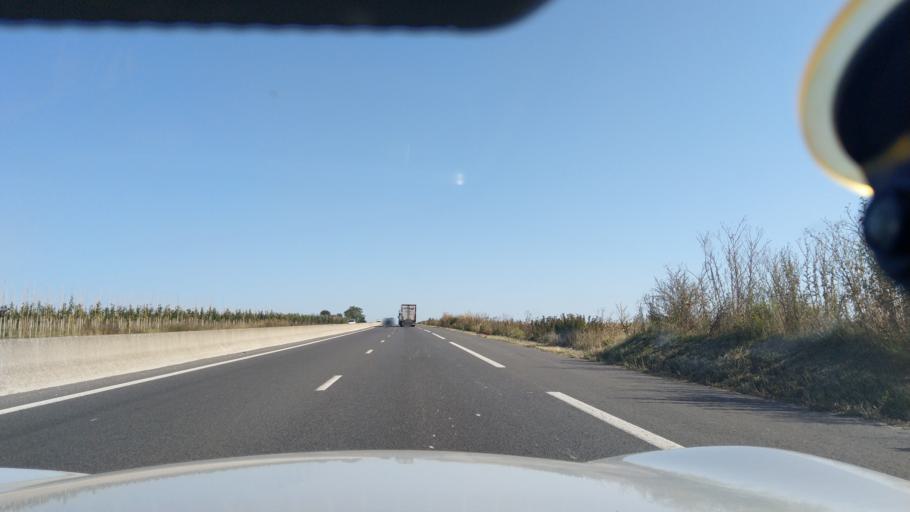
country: FR
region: Ile-de-France
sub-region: Departement du Val-d'Oise
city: Le Thillay
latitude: 48.9867
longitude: 2.4724
